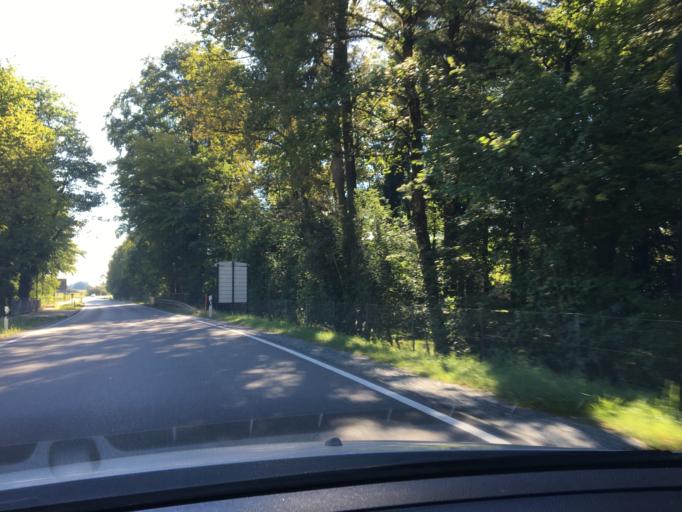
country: DE
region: Bavaria
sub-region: Upper Bavaria
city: Taufkirchen
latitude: 48.3464
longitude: 12.1351
